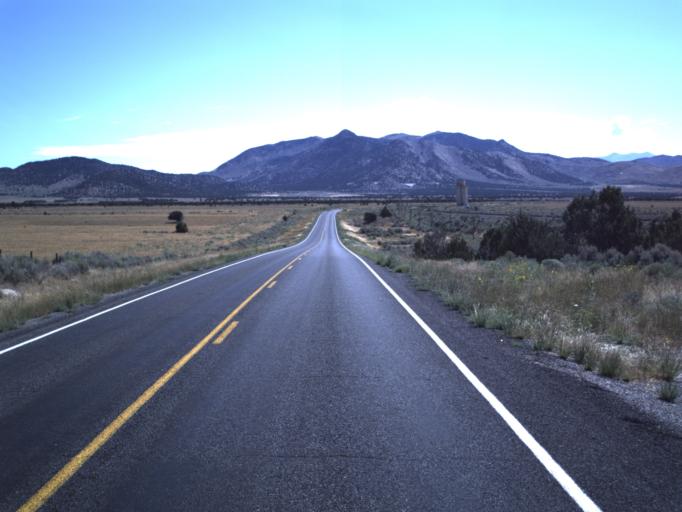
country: US
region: Utah
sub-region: Utah County
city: Genola
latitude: 39.9442
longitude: -112.2071
